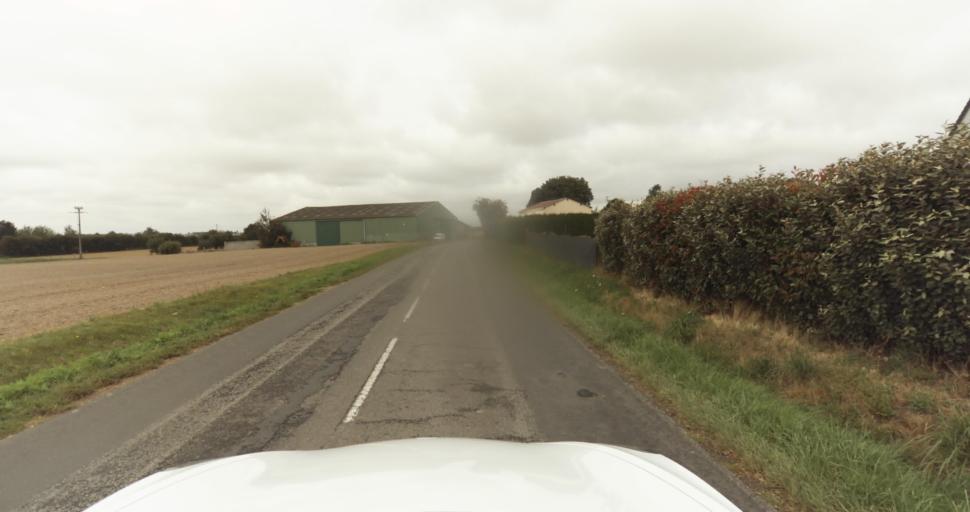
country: FR
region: Haute-Normandie
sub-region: Departement de l'Eure
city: Aviron
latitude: 49.0639
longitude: 1.0723
